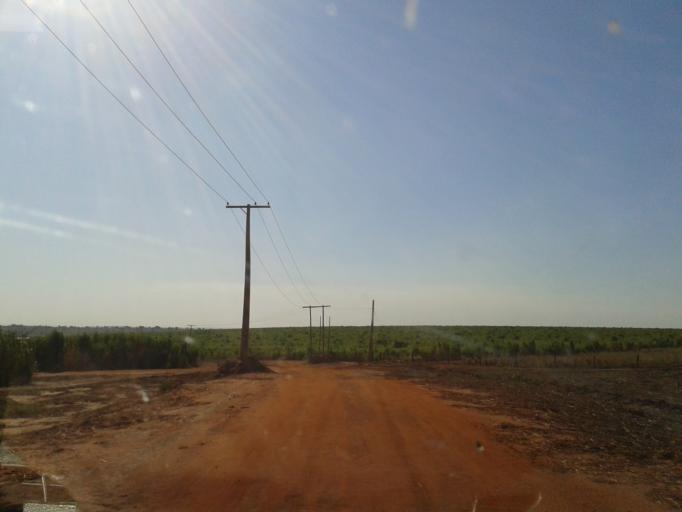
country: BR
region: Minas Gerais
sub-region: Santa Vitoria
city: Santa Vitoria
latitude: -18.7311
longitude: -50.2660
